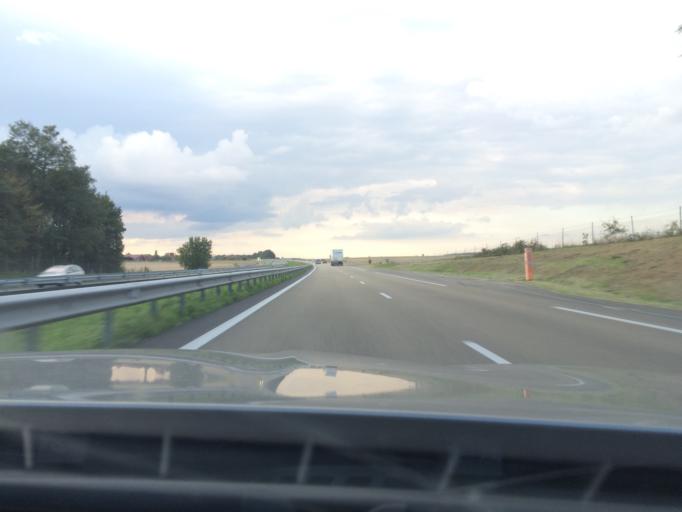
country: FR
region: Ile-de-France
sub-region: Departement de Seine-et-Marne
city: Egreville
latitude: 48.1490
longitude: 2.9028
